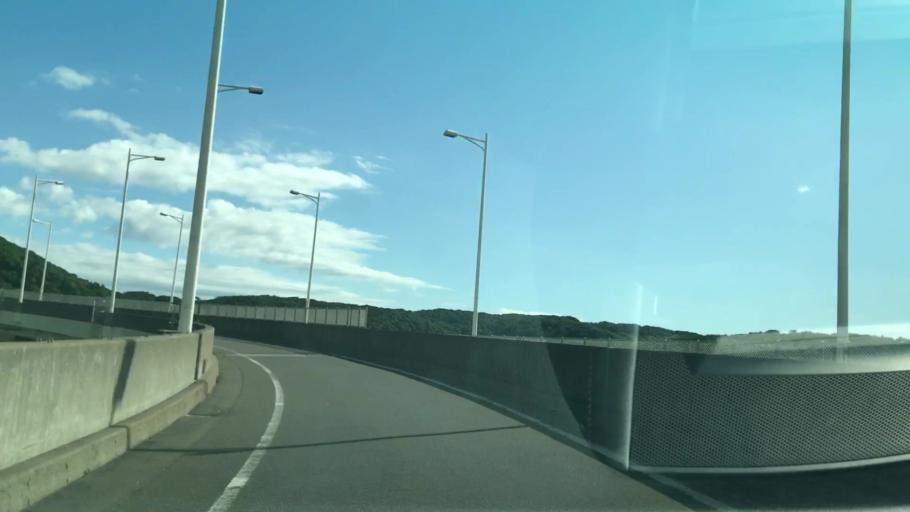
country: JP
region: Hokkaido
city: Muroran
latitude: 42.3418
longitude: 140.9478
